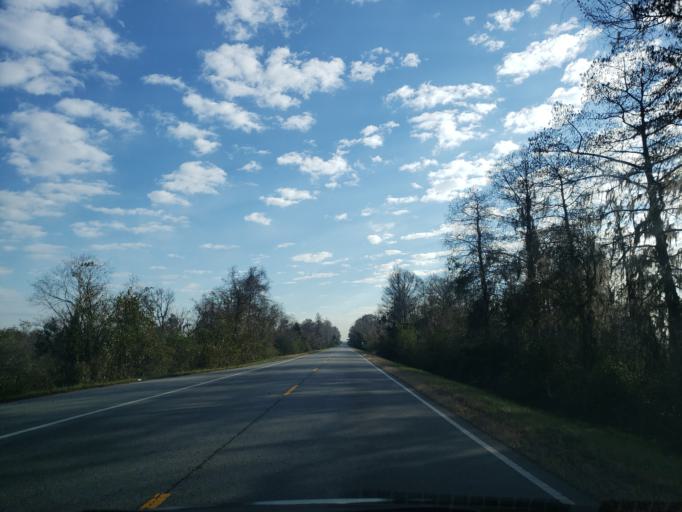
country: US
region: Georgia
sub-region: Chatham County
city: Port Wentworth
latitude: 32.1656
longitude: -81.1466
